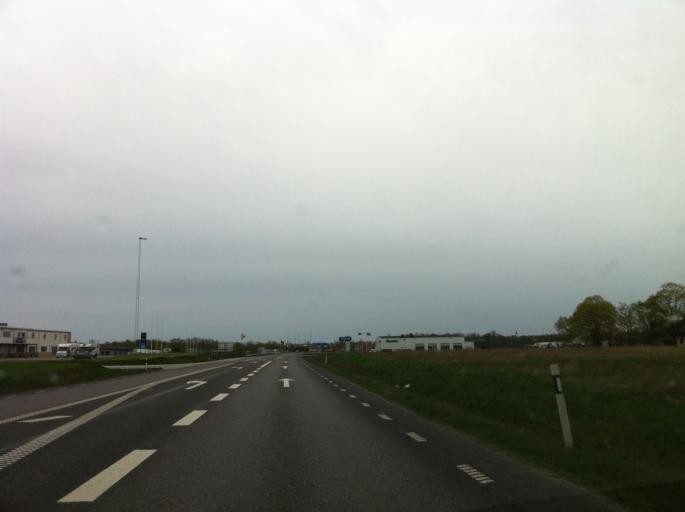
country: SE
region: Halland
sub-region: Falkenbergs Kommun
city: Falkenberg
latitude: 56.9393
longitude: 12.5236
